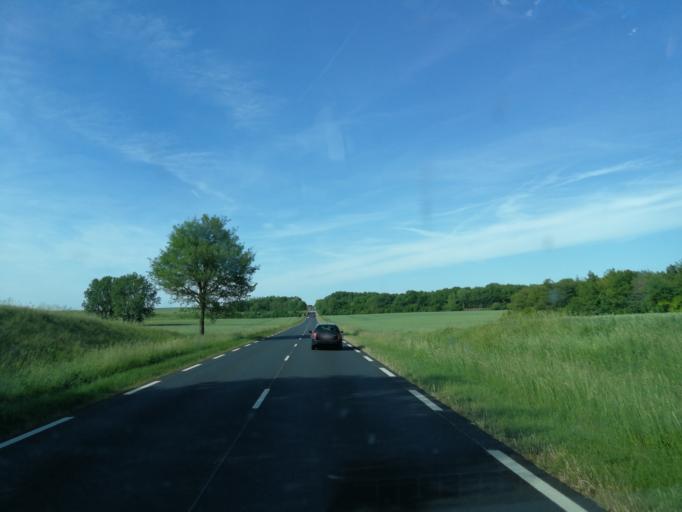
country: FR
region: Centre
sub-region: Departement du Loir-et-Cher
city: Saint-Amand-Longpre
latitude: 47.7232
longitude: 1.0213
